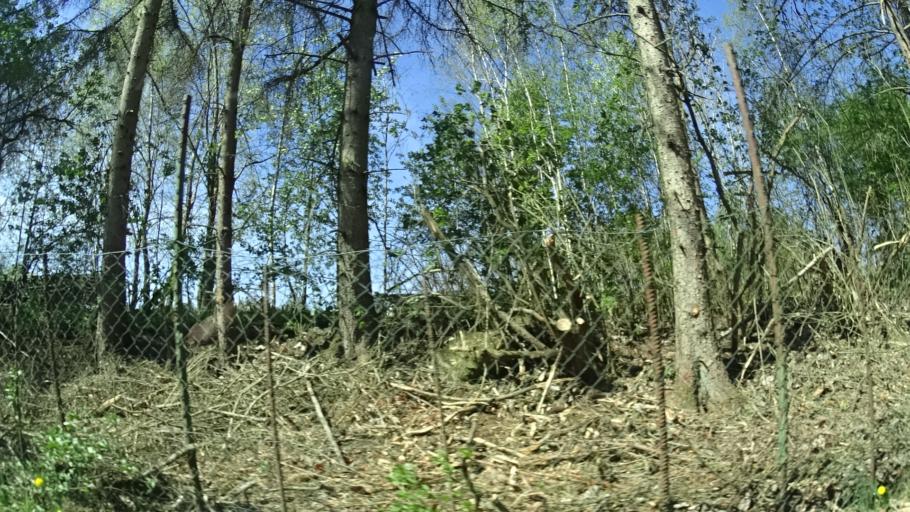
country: DE
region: Thuringia
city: Veilsdorf
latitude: 50.3040
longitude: 10.8008
